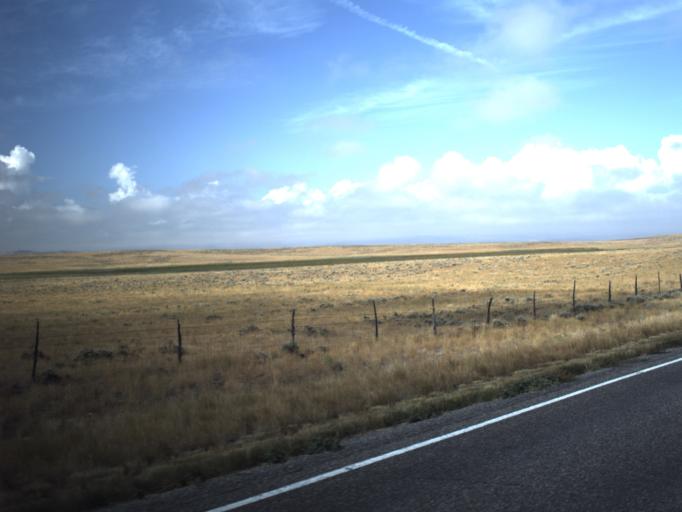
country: US
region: Wyoming
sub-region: Uinta County
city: Evanston
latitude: 41.4326
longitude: -111.0630
